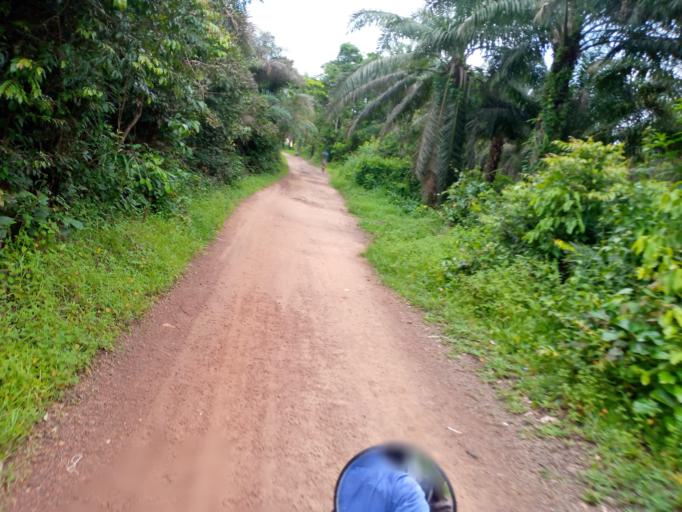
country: SL
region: Northern Province
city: Mange
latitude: 8.9902
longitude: -12.7935
